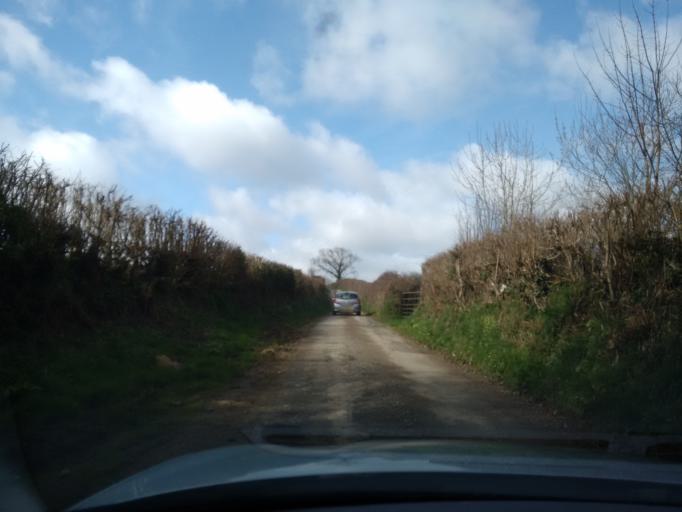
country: GB
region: England
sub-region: Cornwall
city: Launceston
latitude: 50.6003
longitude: -4.3437
